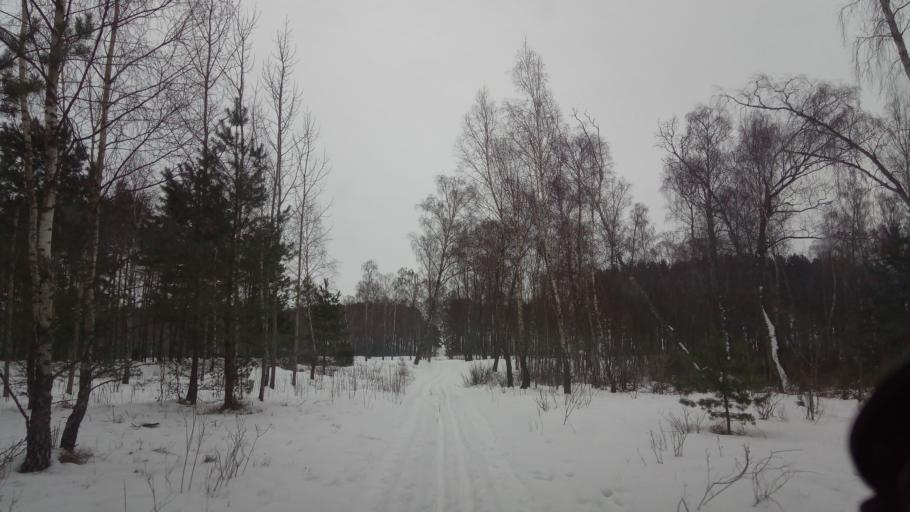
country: LT
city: Neringa
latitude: 55.4183
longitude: 21.0995
